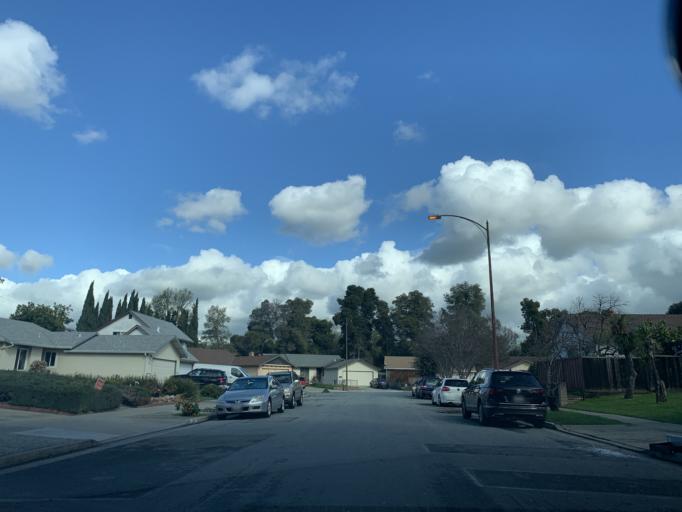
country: US
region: California
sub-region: Santa Clara County
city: Milpitas
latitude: 37.3936
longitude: -121.8752
